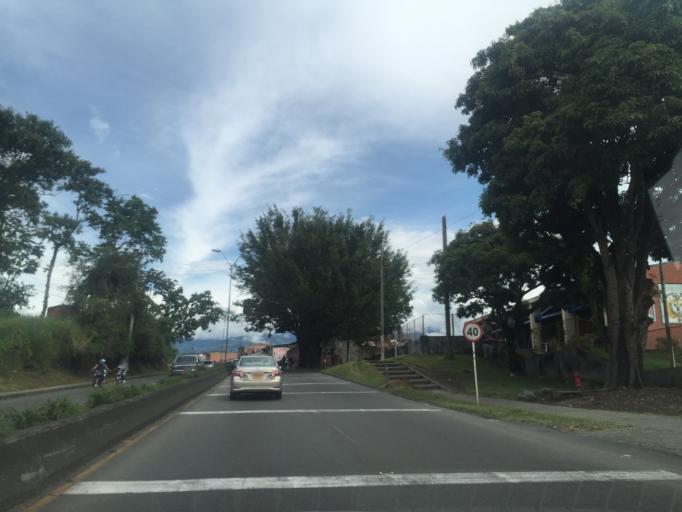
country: CO
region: Quindio
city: Armenia
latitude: 4.5316
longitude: -75.6896
